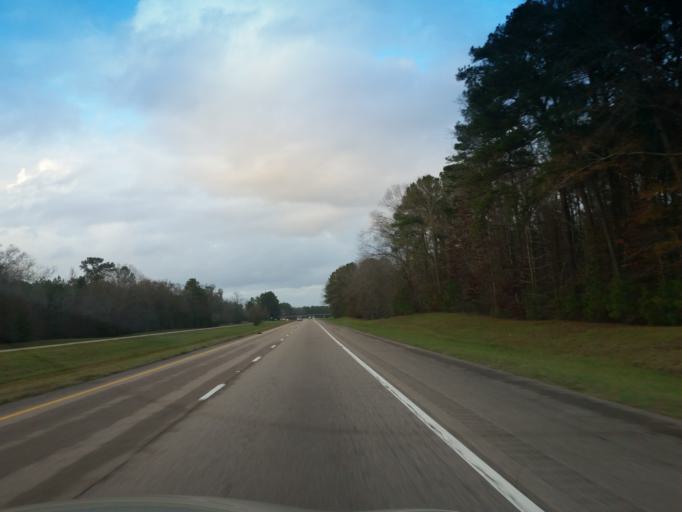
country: US
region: Mississippi
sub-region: Clarke County
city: Stonewall
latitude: 32.0310
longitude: -88.9218
